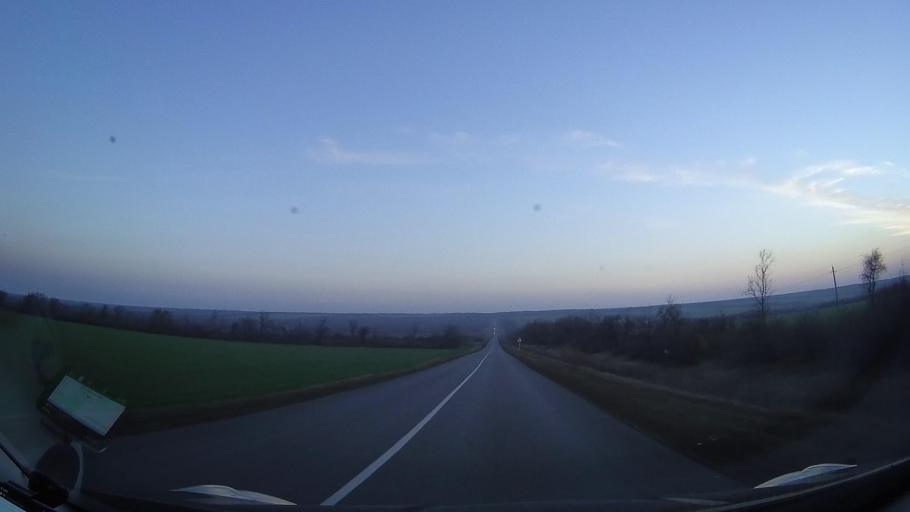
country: RU
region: Rostov
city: Zernograd
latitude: 46.9055
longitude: 40.3389
